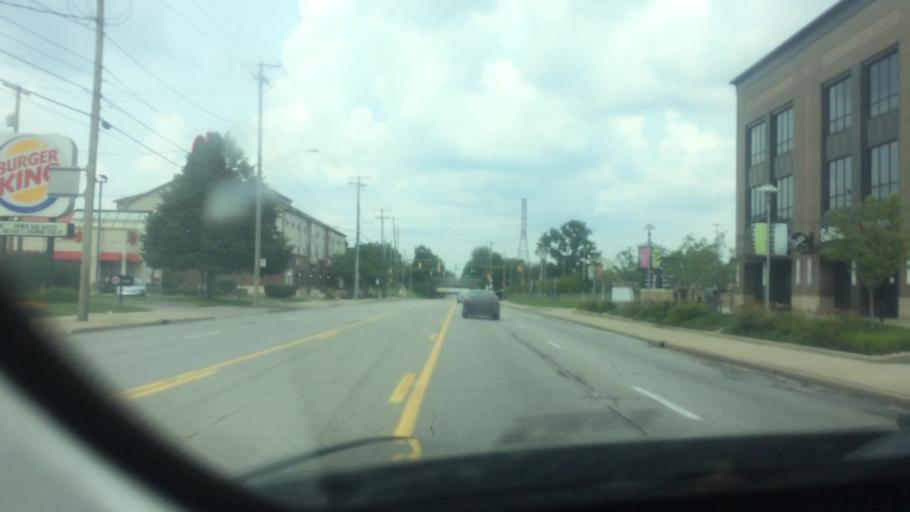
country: US
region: Ohio
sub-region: Lucas County
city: Ottawa Hills
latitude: 41.6538
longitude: -83.6218
